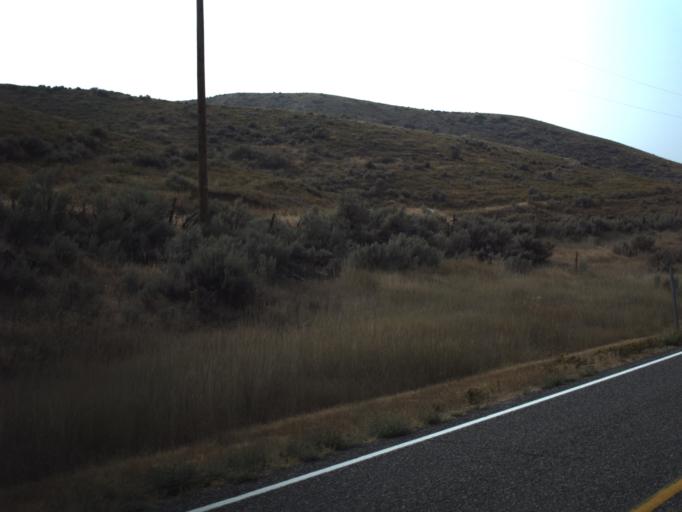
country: US
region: Utah
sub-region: Summit County
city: Coalville
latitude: 41.0003
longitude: -111.5219
